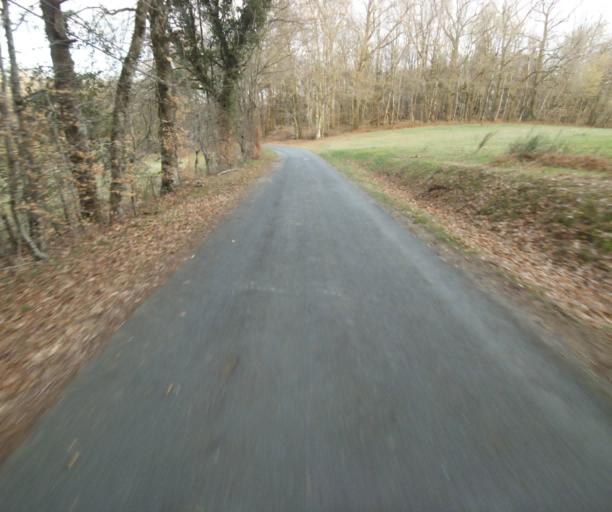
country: FR
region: Limousin
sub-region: Departement de la Correze
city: Uzerche
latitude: 45.3662
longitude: 1.5905
